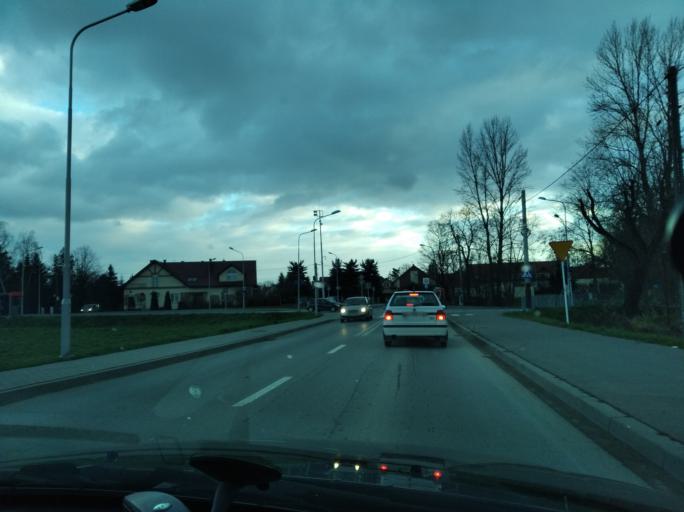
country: PL
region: Subcarpathian Voivodeship
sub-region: Rzeszow
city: Rzeszow
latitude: 50.0273
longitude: 22.0423
